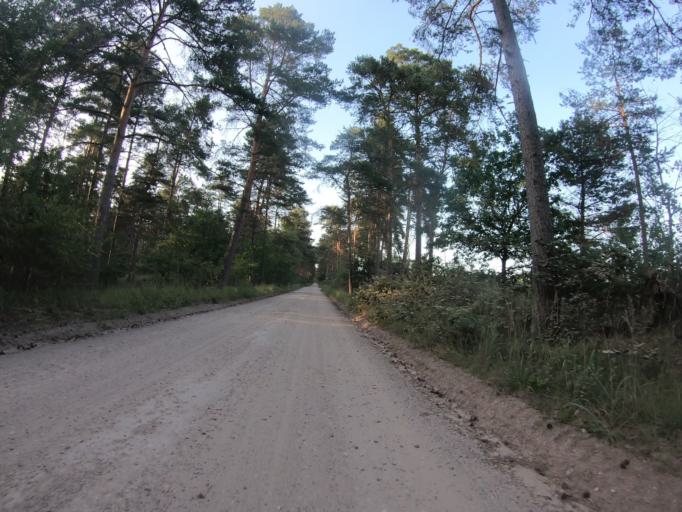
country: DE
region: Lower Saxony
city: Wagenhoff
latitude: 52.5399
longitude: 10.4967
